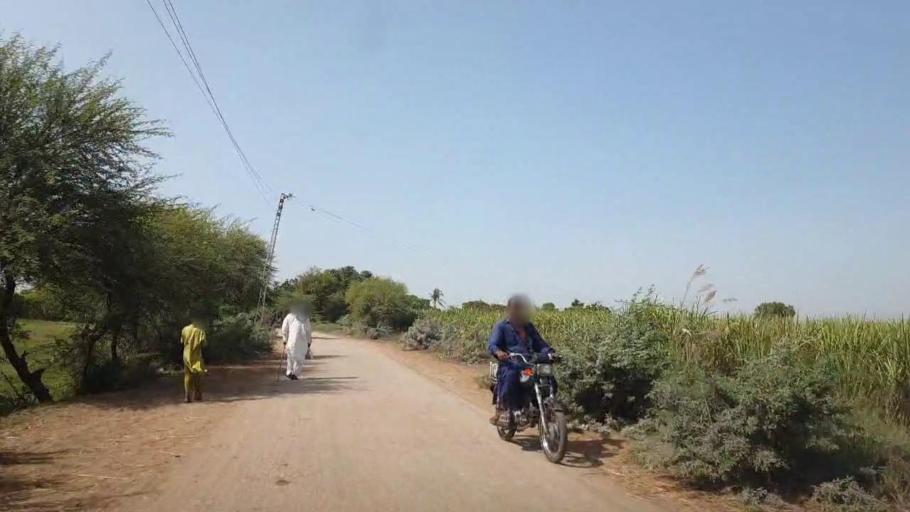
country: PK
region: Sindh
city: Tando Muhammad Khan
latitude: 25.1595
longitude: 68.3824
